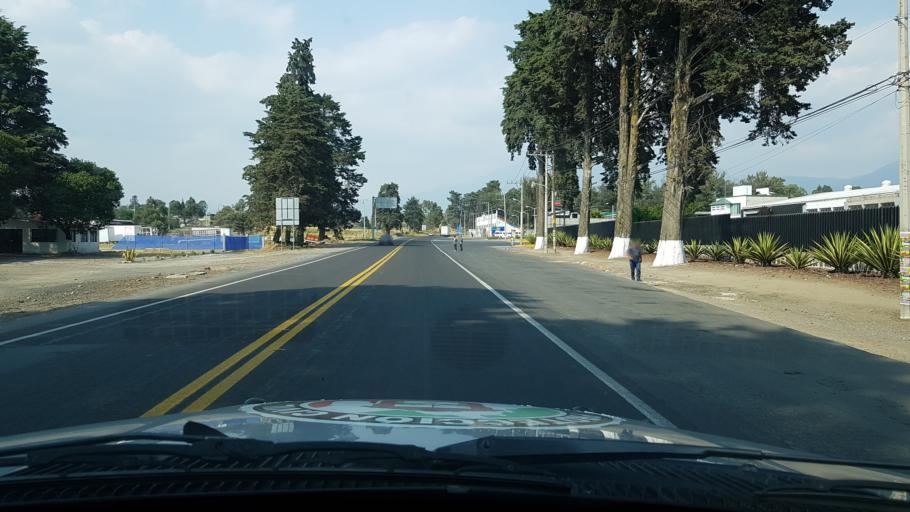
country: MX
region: Mexico
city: Ozumba de Alzate
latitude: 19.0363
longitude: -98.8085
